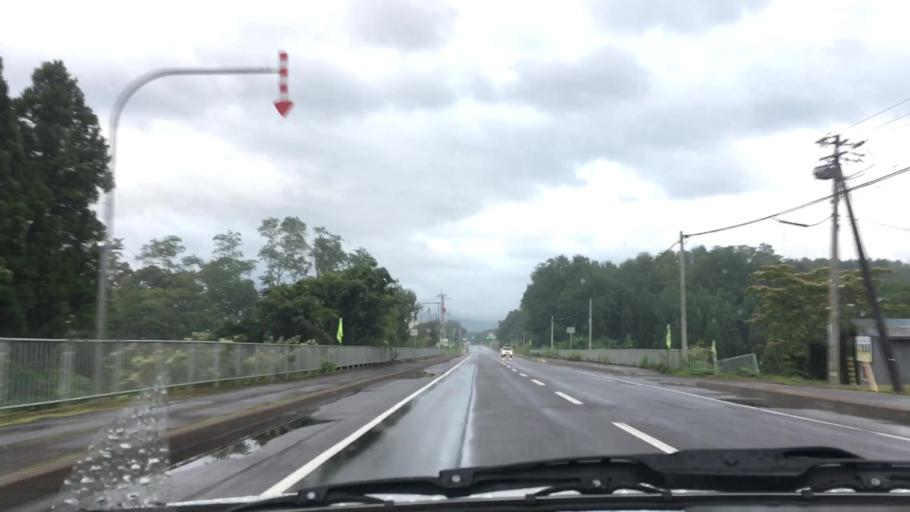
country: JP
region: Hokkaido
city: Nanae
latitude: 42.1140
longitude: 140.5441
